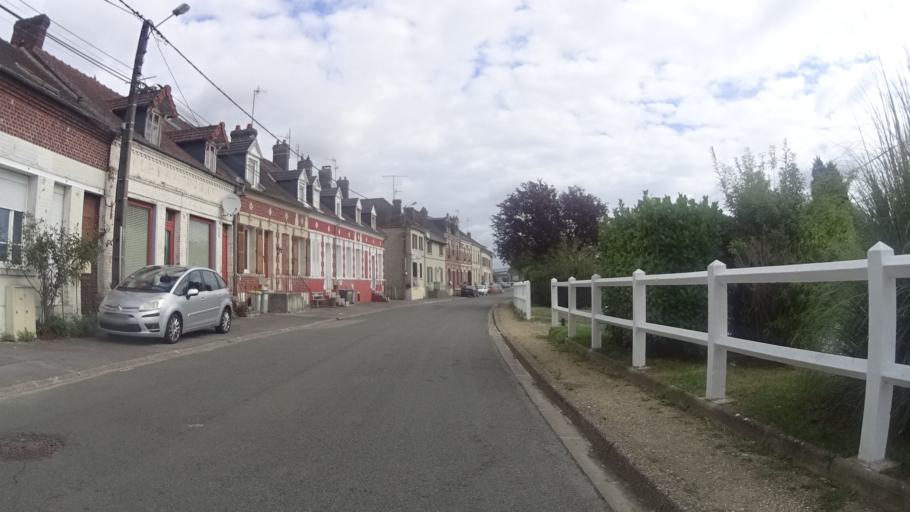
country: FR
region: Picardie
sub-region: Departement de l'Oise
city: Longueil-Annel
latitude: 49.4623
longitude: 2.8618
